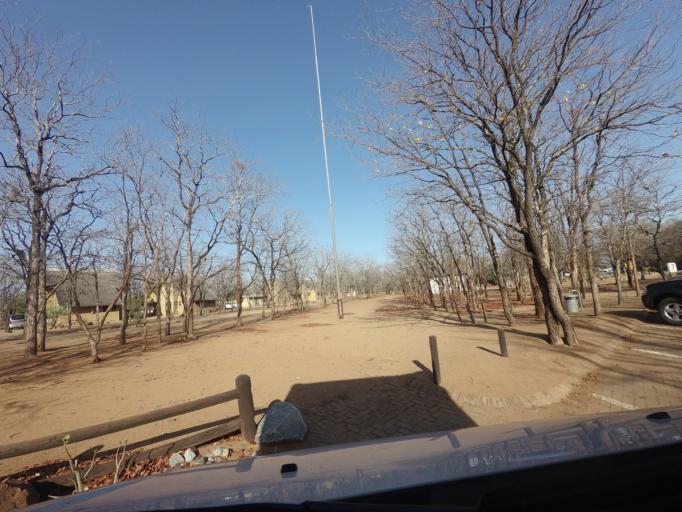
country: ZA
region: Limpopo
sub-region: Mopani District Municipality
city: Giyani
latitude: -23.1086
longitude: 31.4352
